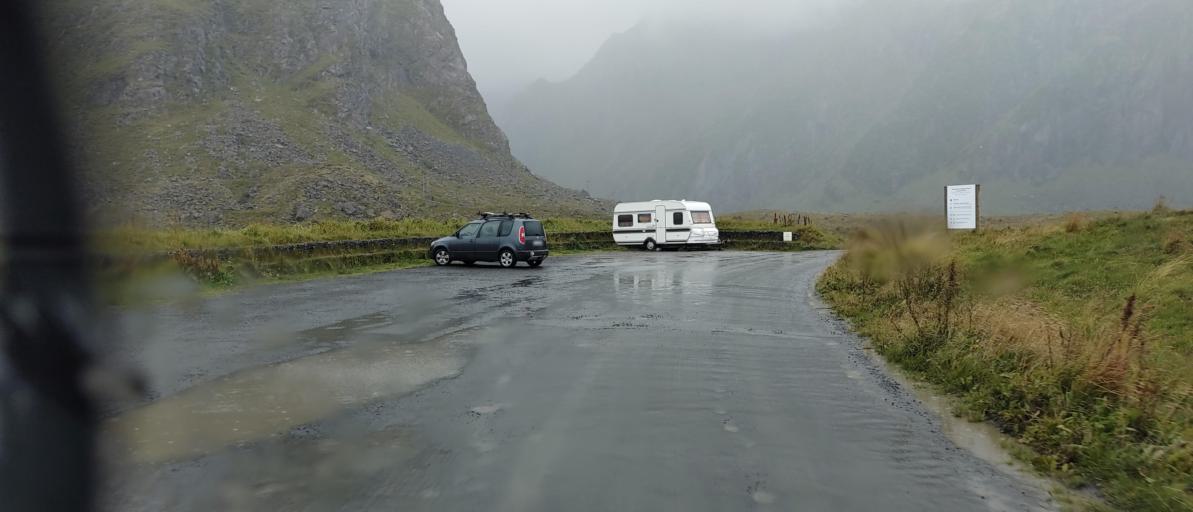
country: NO
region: Nordland
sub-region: Vestvagoy
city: Evjen
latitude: 68.3082
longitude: 13.6541
